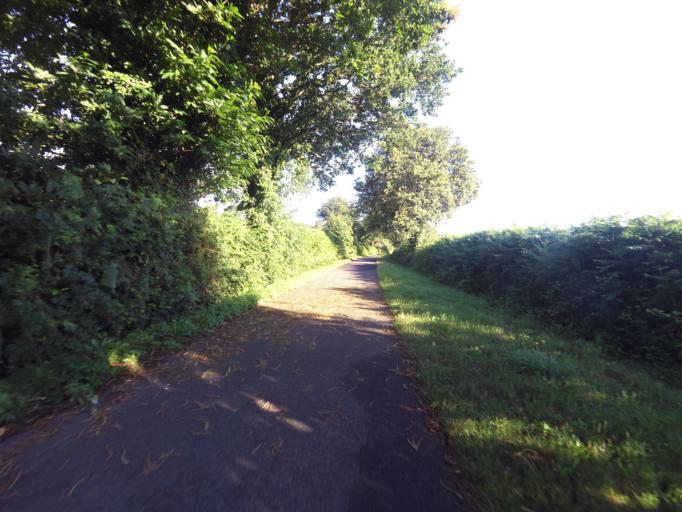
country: FR
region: Brittany
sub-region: Departement du Morbihan
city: Malestroit
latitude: 47.8178
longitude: -2.4155
